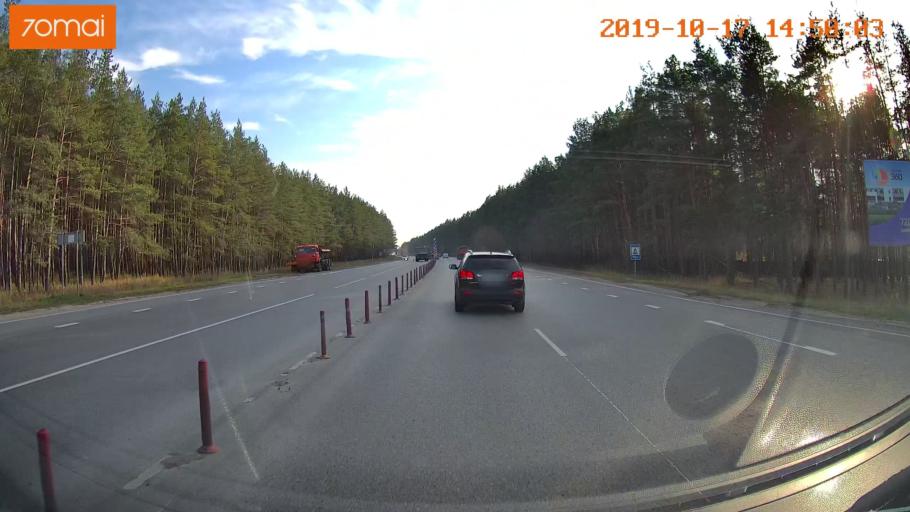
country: RU
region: Rjazan
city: Polyany
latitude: 54.7390
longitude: 39.8409
